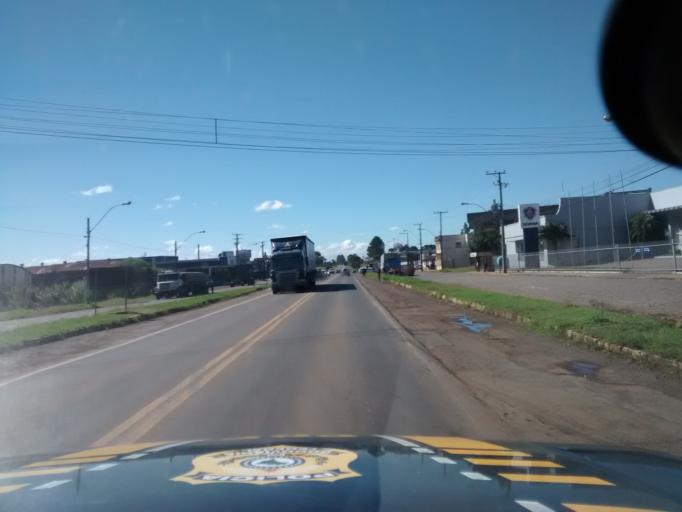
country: BR
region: Rio Grande do Sul
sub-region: Vacaria
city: Vacaria
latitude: -28.5084
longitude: -50.9283
